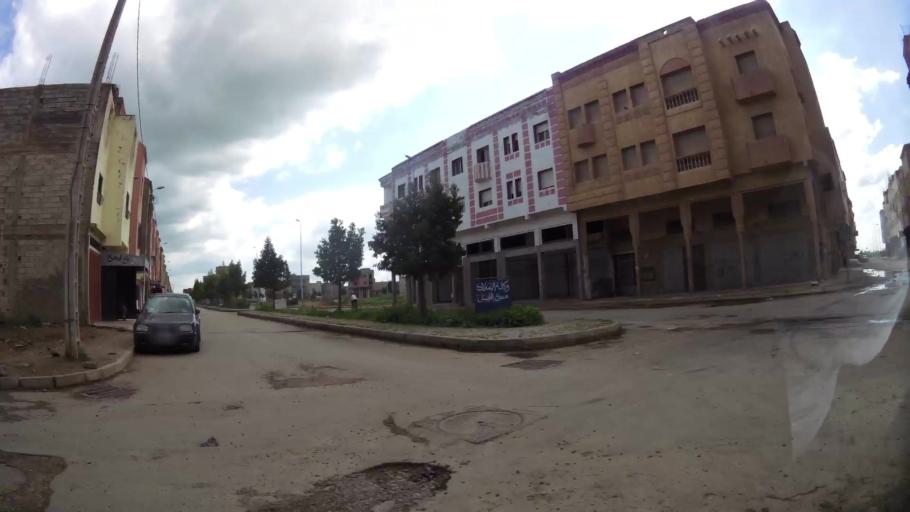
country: MA
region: Grand Casablanca
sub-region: Mediouna
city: Mediouna
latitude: 33.3694
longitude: -7.5301
